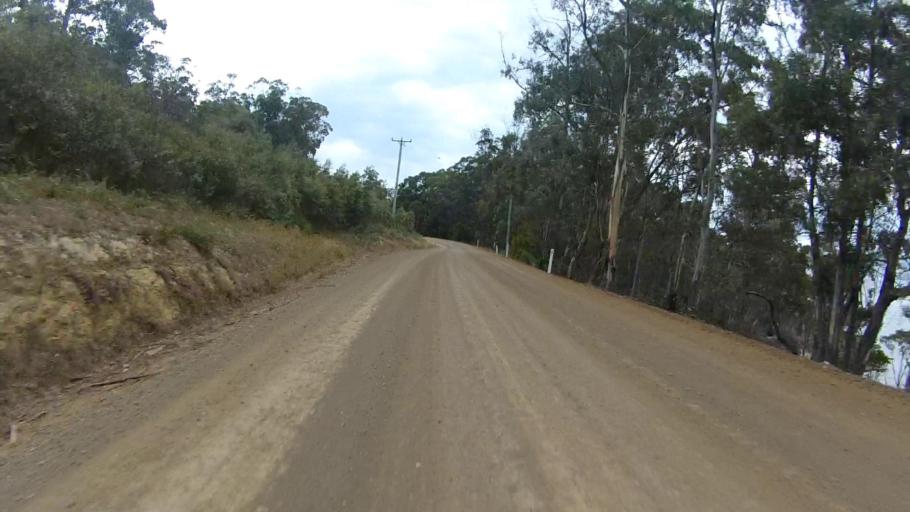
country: AU
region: Tasmania
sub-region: Huon Valley
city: Cygnet
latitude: -43.2216
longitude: 147.0923
